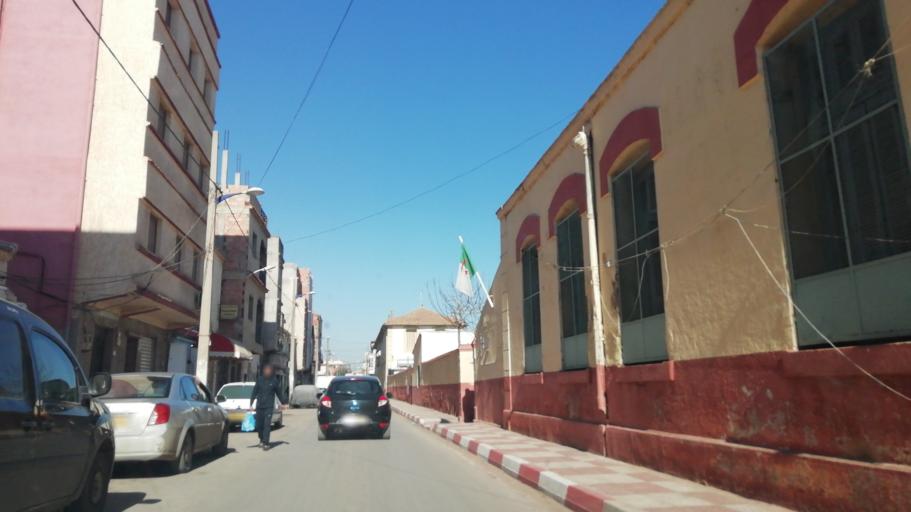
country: DZ
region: Oran
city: Es Senia
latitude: 35.6502
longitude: -0.6244
